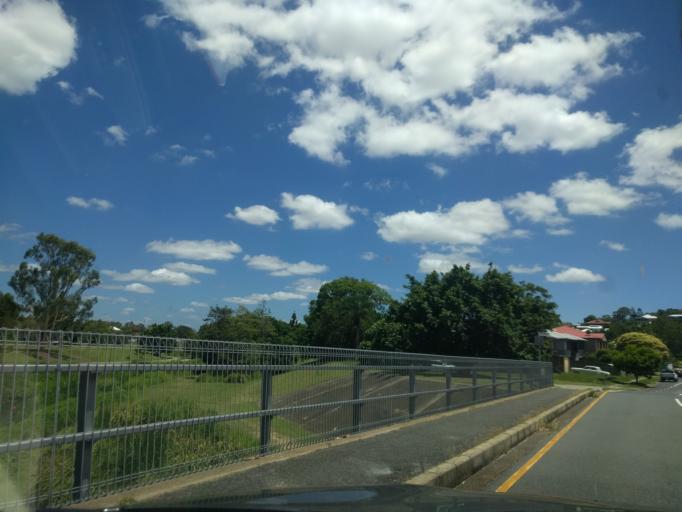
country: AU
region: Queensland
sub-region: Brisbane
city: Gordon Park
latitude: -27.4220
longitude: 153.0241
